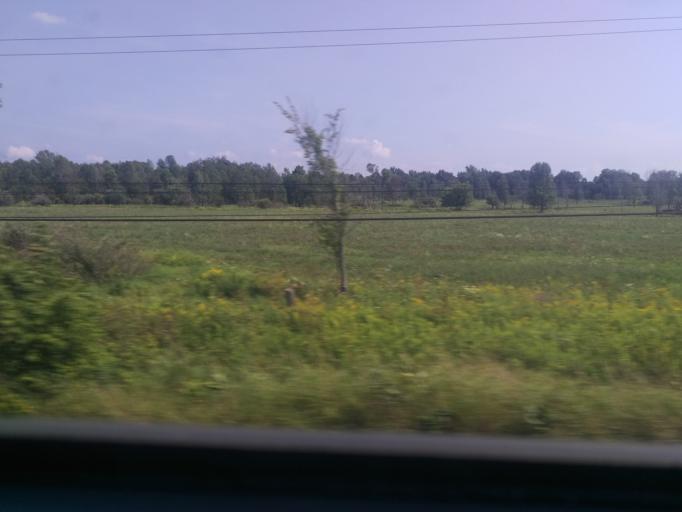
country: US
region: New York
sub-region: Jefferson County
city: Alexandria Bay
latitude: 44.4740
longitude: -75.8920
